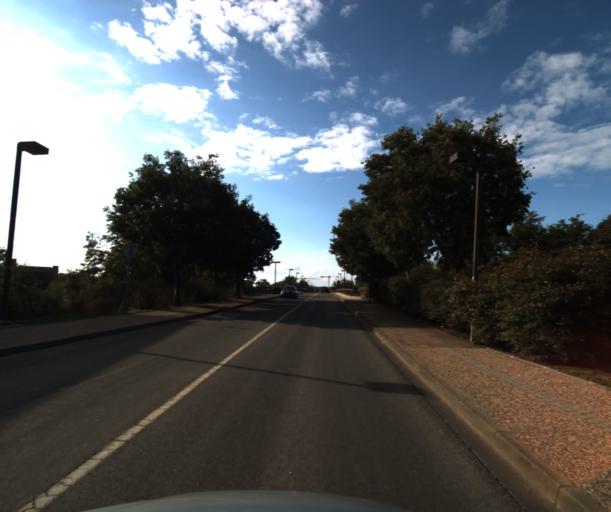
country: FR
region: Midi-Pyrenees
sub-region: Departement de la Haute-Garonne
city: Muret
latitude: 43.4601
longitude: 1.3344
